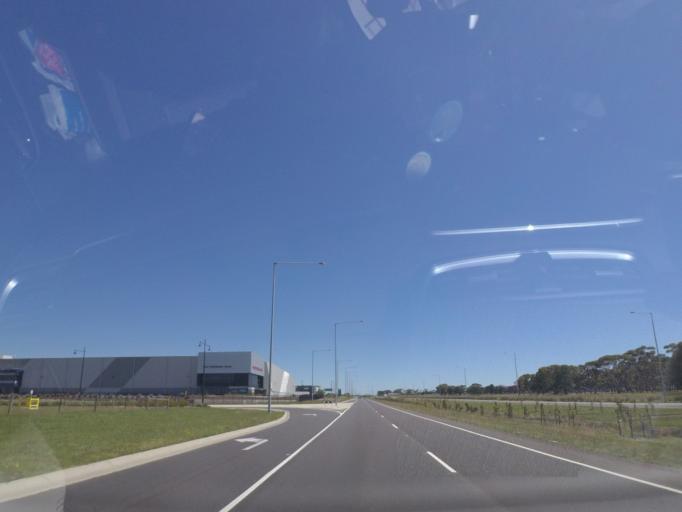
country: AU
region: Victoria
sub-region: Hume
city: Tullamarine
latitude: -37.6977
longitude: 144.8668
